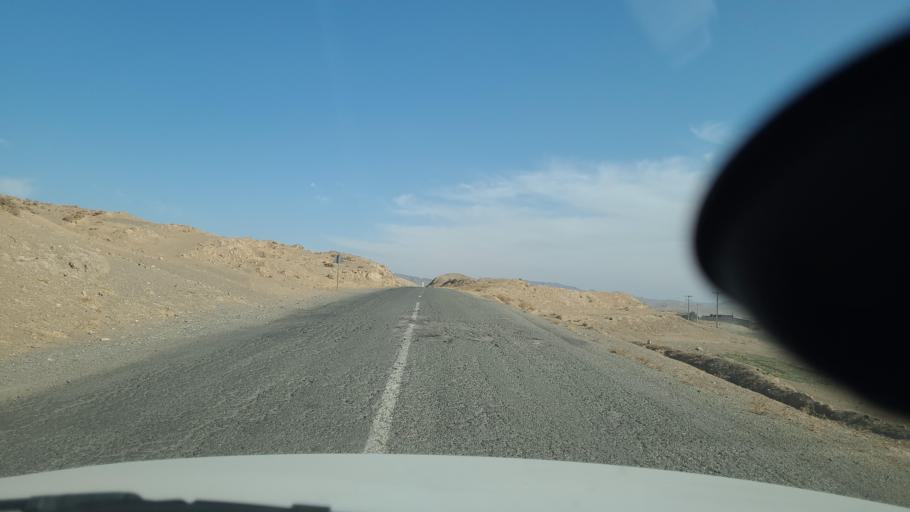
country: IR
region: Razavi Khorasan
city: Fariman
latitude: 35.5911
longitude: 59.6729
